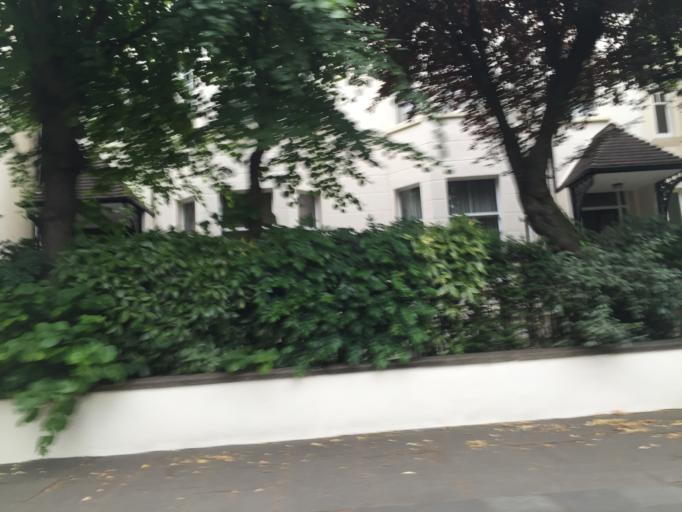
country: GB
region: England
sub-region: Greater London
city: Belsize Park
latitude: 51.5339
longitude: -0.1793
